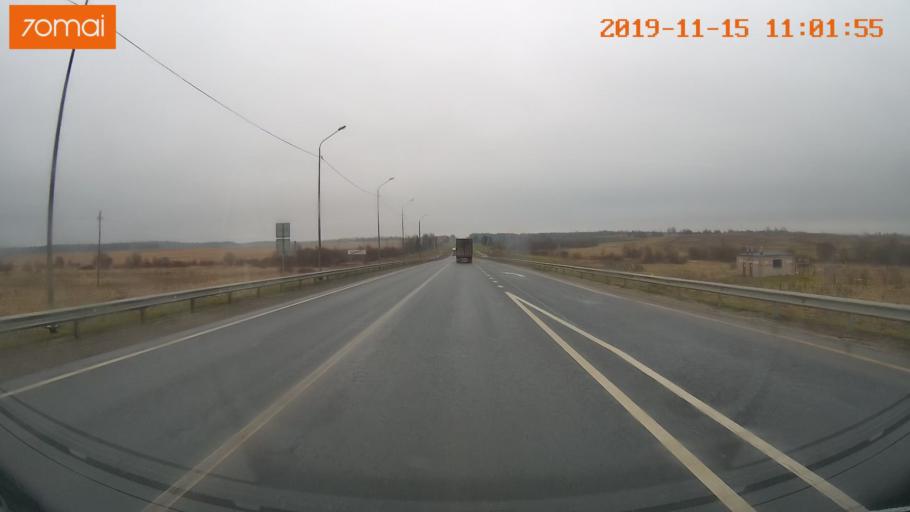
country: RU
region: Vologda
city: Chebsara
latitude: 59.1309
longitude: 38.9302
